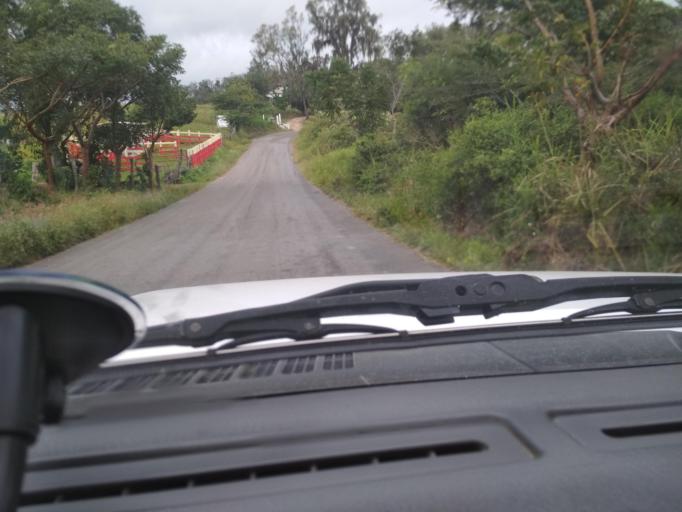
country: MX
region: Veracruz
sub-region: Emiliano Zapata
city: Dos Rios
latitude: 19.5338
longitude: -96.8008
